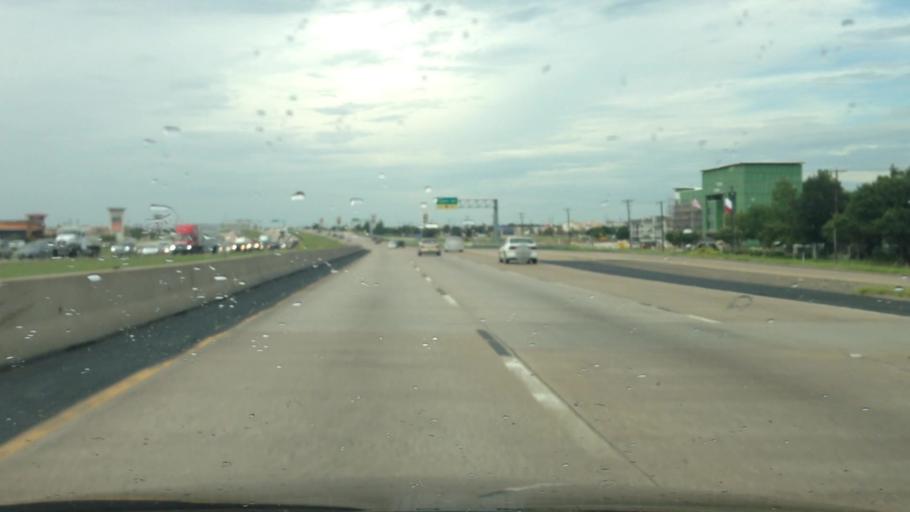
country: US
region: Texas
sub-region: Tarrant County
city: Euless
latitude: 32.8707
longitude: -97.0999
